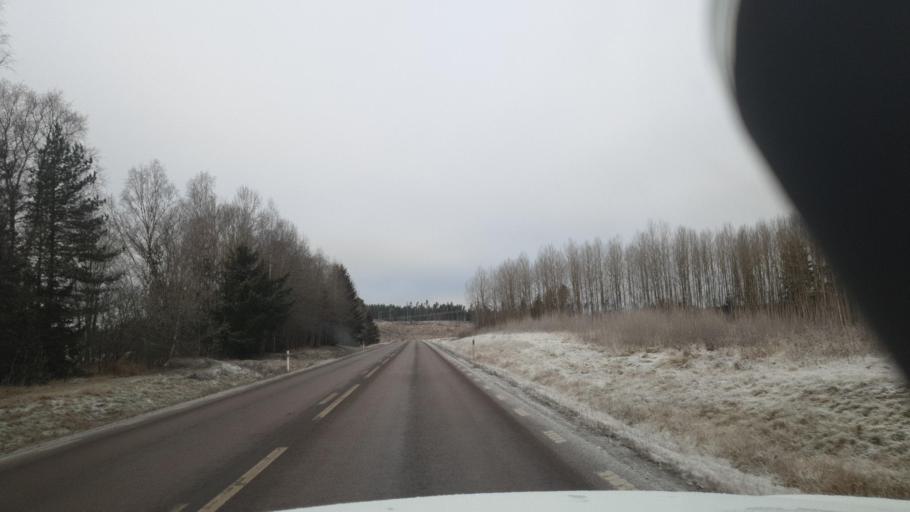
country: SE
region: Vaermland
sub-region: Karlstads Kommun
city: Edsvalla
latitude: 59.5206
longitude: 13.1611
